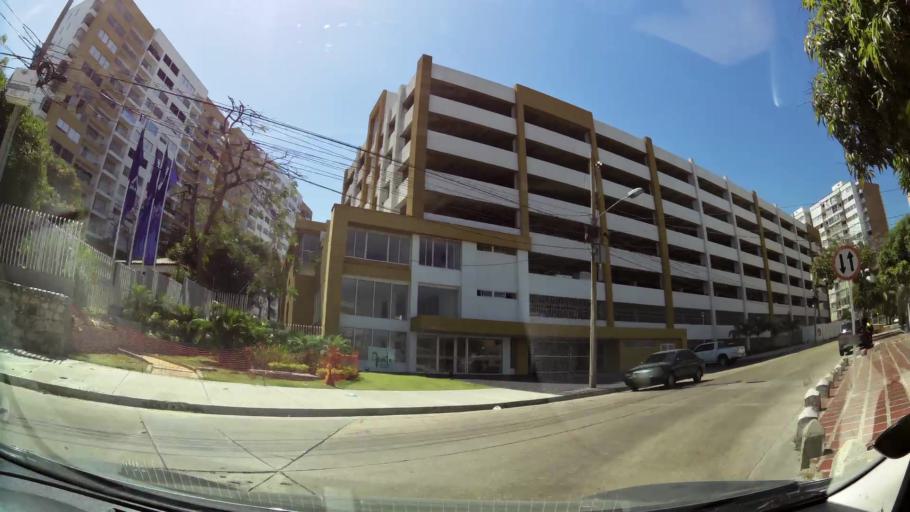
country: CO
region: Atlantico
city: Barranquilla
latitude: 10.9916
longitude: -74.8109
